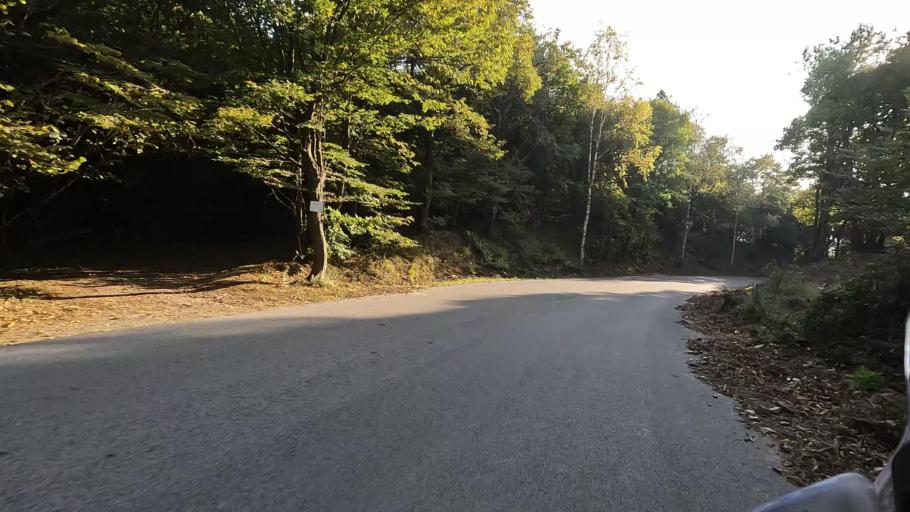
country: IT
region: Liguria
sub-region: Provincia di Savona
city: San Giovanni
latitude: 44.4120
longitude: 8.5292
